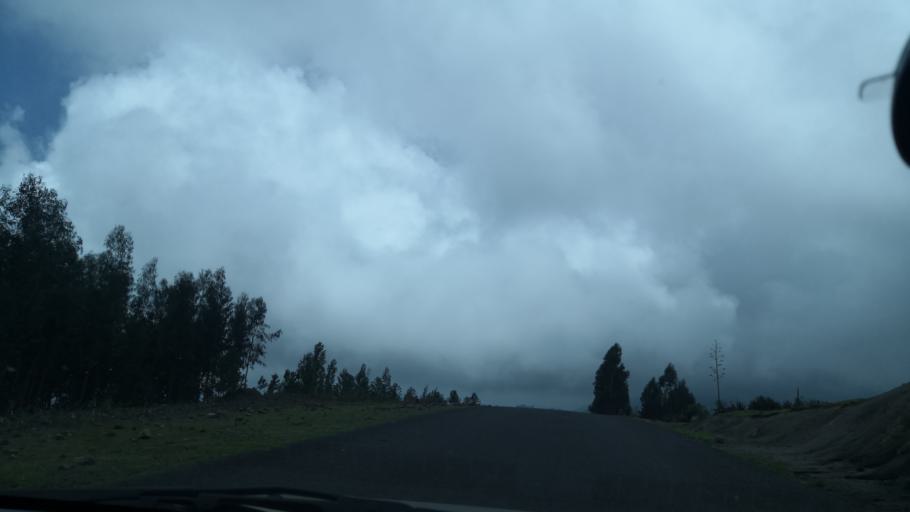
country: ET
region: Amhara
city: Kemise
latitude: 10.3405
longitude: 39.8408
